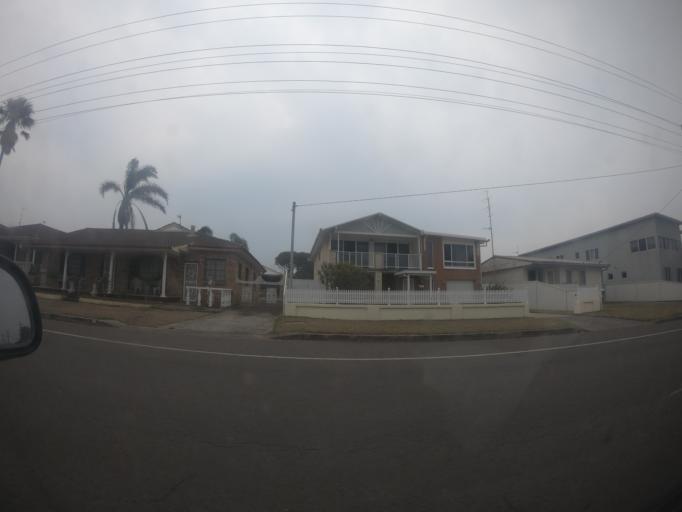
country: AU
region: New South Wales
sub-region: Shellharbour
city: Lake Illawarra
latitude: -34.5502
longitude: 150.8678
